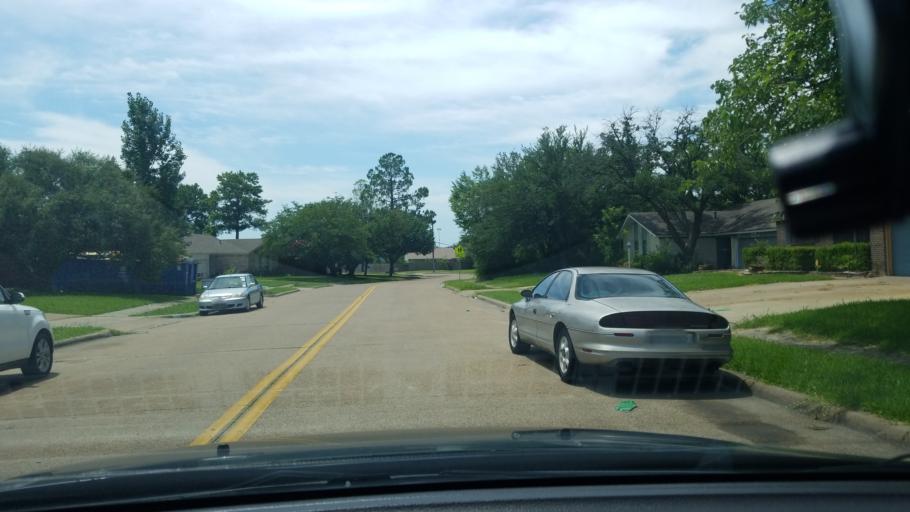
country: US
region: Texas
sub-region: Dallas County
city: Mesquite
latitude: 32.8029
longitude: -96.6573
